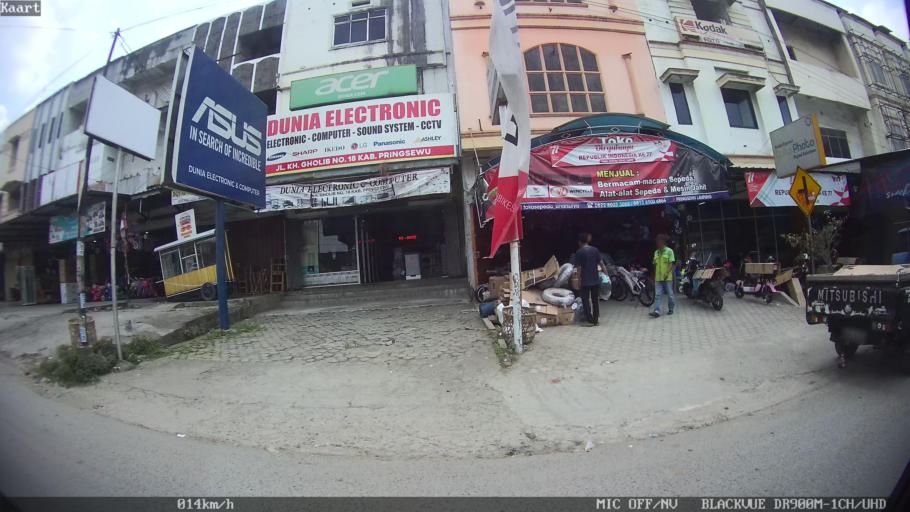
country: ID
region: Lampung
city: Pringsewu
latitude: -5.3551
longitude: 104.9769
